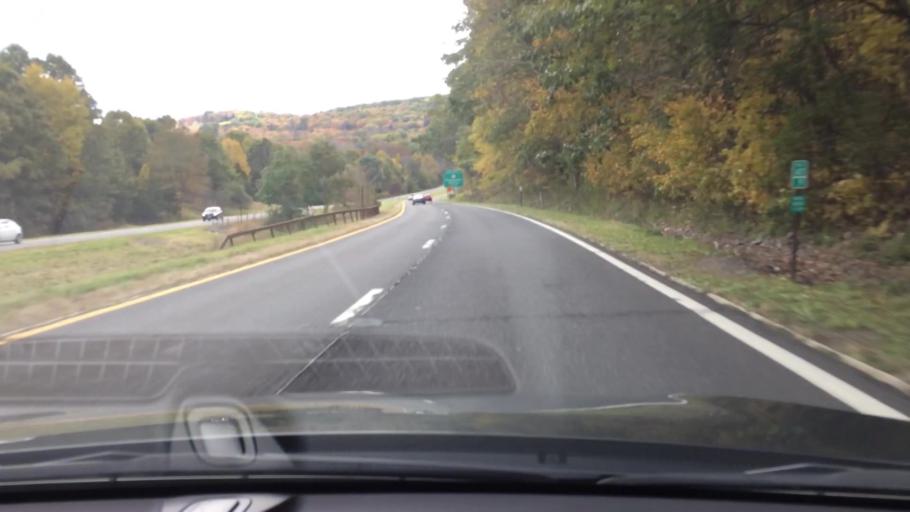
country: US
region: New York
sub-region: Dutchess County
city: Hillside Lake
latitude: 41.6785
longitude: -73.7877
